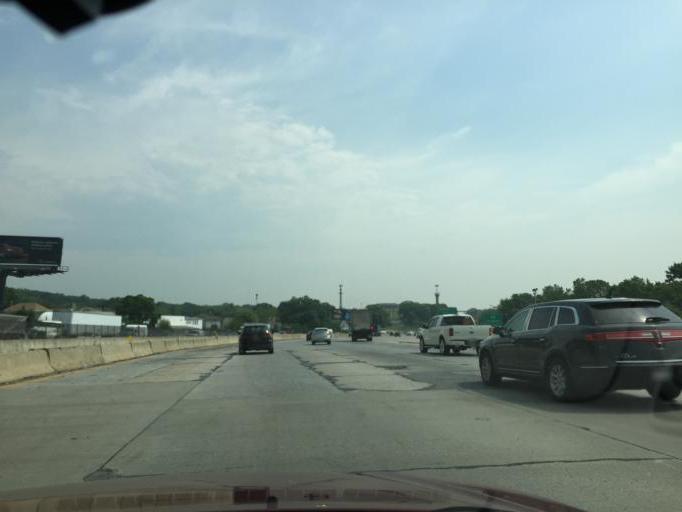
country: US
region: New York
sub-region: Westchester County
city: Larchmont
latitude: 40.9269
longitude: -73.7699
